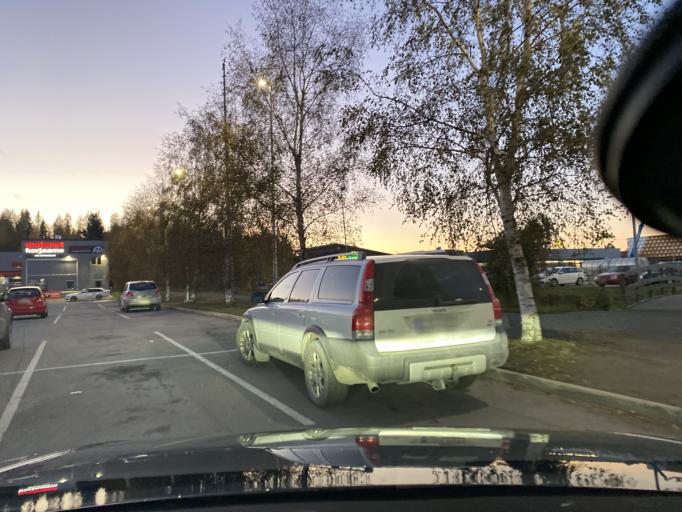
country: FI
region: Pirkanmaa
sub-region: Tampere
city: Tampere
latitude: 61.4678
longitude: 23.7175
